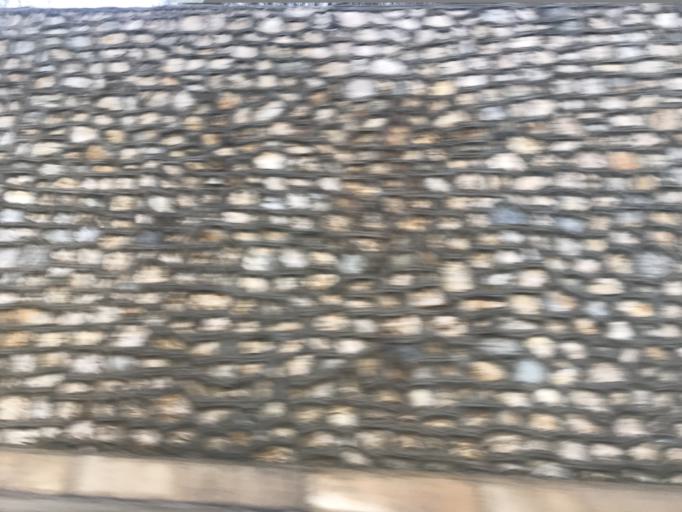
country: TR
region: Bartin
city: Amasra
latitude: 41.7298
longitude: 32.3823
